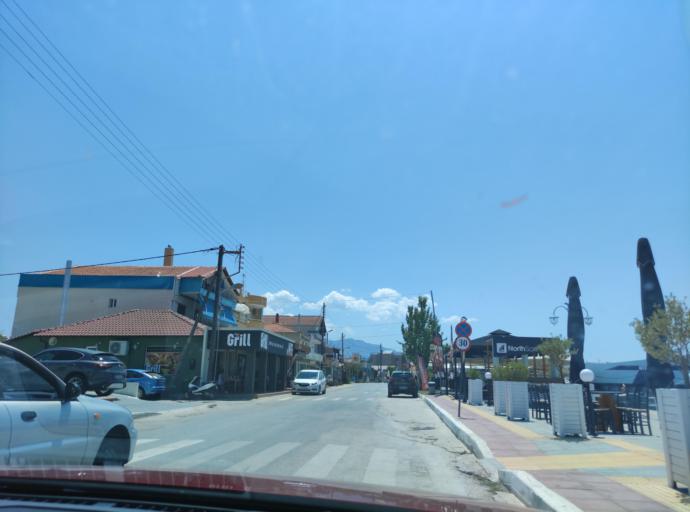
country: GR
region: East Macedonia and Thrace
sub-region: Nomos Kavalas
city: Keramoti
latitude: 40.8581
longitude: 24.7035
